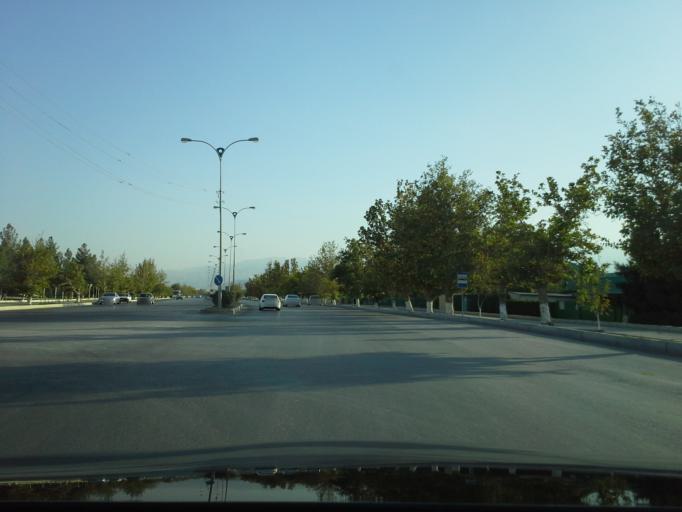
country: TM
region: Ahal
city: Abadan
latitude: 38.0428
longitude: 58.1857
